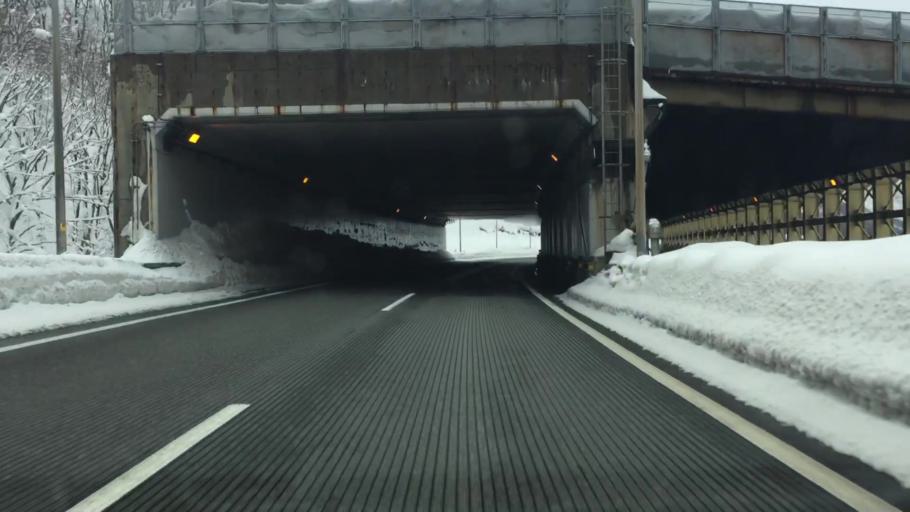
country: JP
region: Niigata
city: Shiozawa
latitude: 36.8676
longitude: 138.8688
